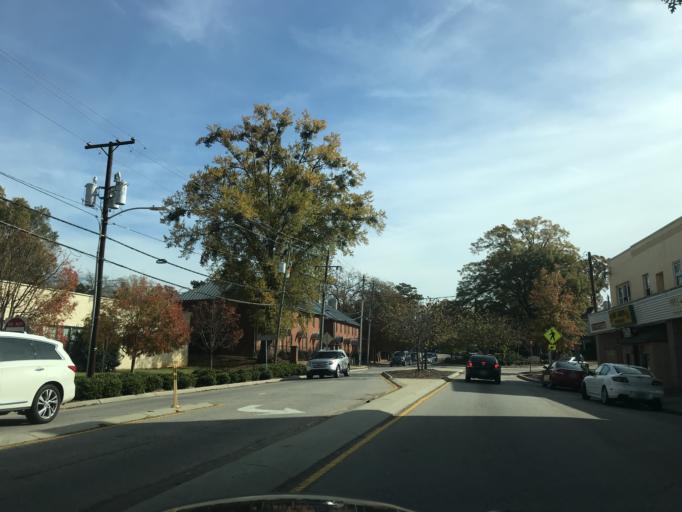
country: US
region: North Carolina
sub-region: Wake County
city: West Raleigh
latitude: 35.7831
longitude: -78.6558
